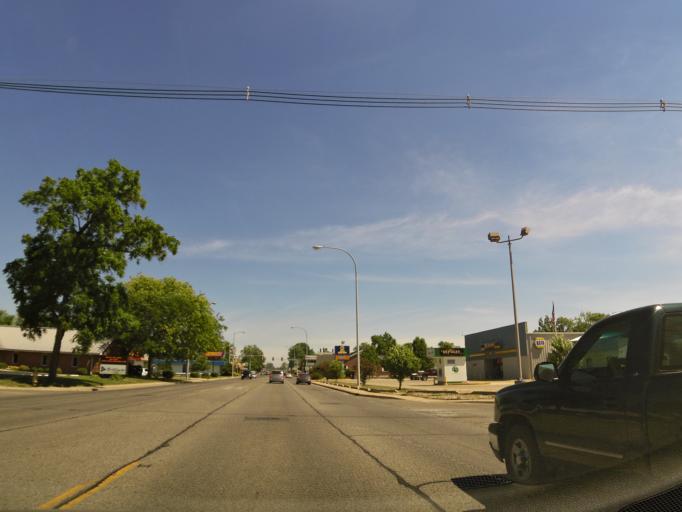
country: US
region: Illinois
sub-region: Vermilion County
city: Danville
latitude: 40.1288
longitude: -87.6356
